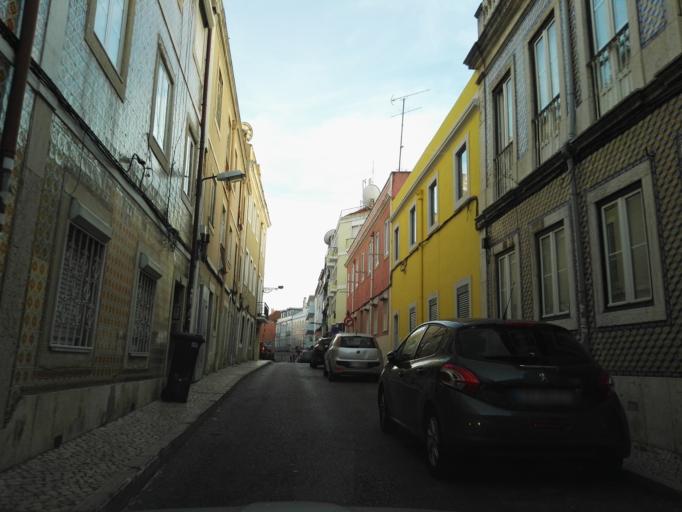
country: PT
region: Lisbon
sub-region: Lisbon
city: Lisbon
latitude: 38.7195
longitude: -9.1613
